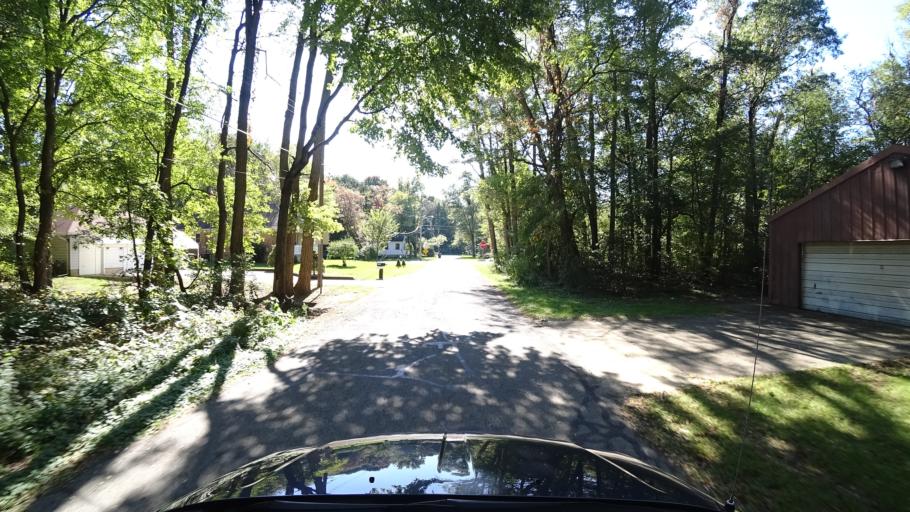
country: US
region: Indiana
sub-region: LaPorte County
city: Michigan City
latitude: 41.6856
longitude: -86.8916
